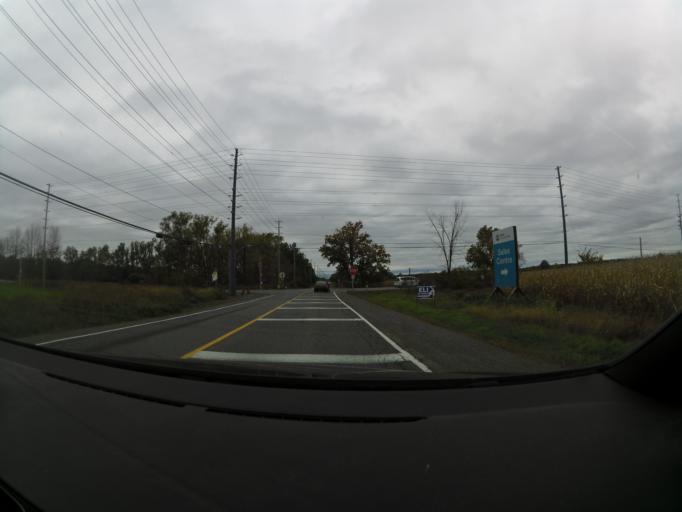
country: CA
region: Ontario
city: Bells Corners
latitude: 45.3091
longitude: -75.9459
